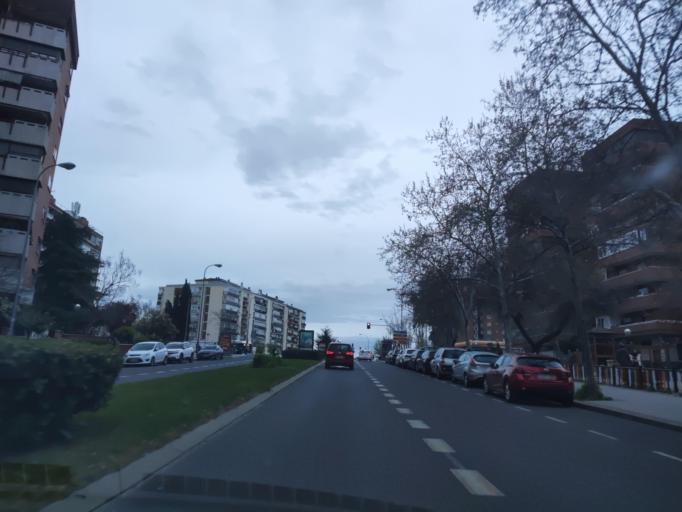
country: ES
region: Madrid
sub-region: Provincia de Madrid
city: Hortaleza
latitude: 40.4661
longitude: -3.6364
